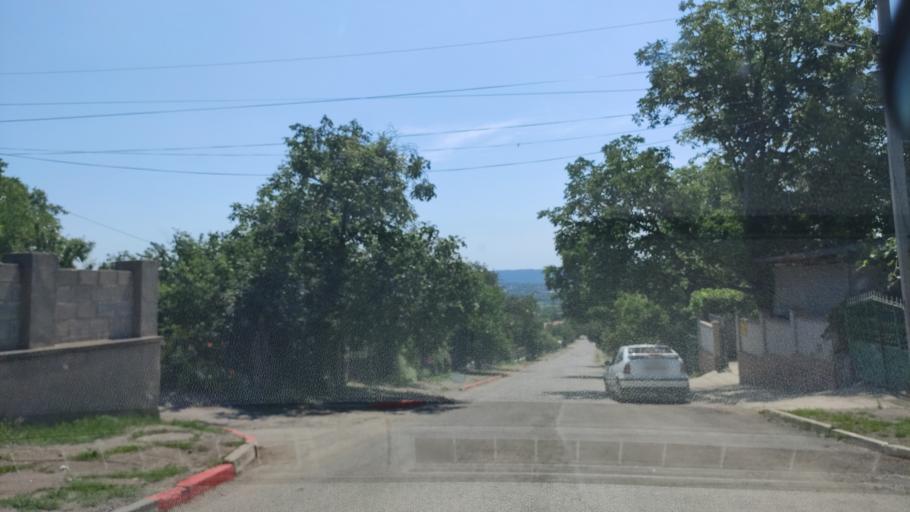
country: MD
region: Raionul Soroca
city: Soroca
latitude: 48.1720
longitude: 28.2964
